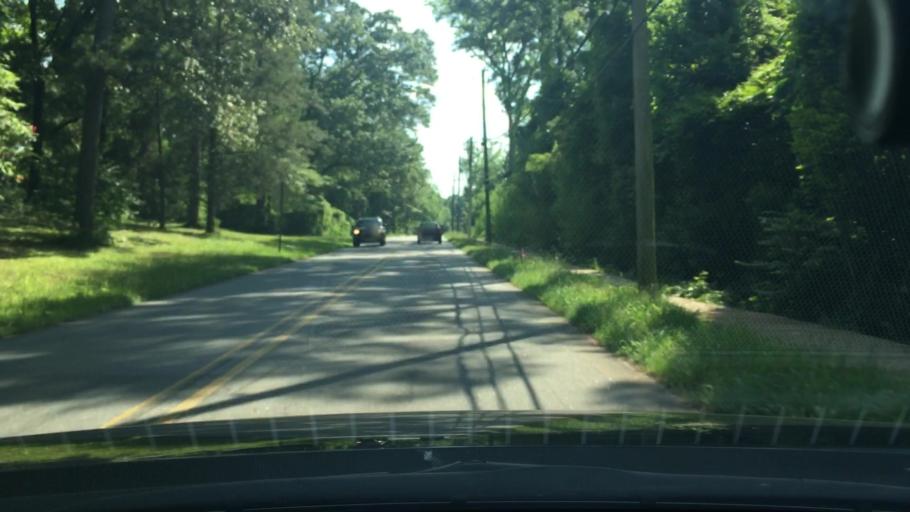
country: US
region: Georgia
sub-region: Spalding County
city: Experiment
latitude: 33.2454
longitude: -84.2892
